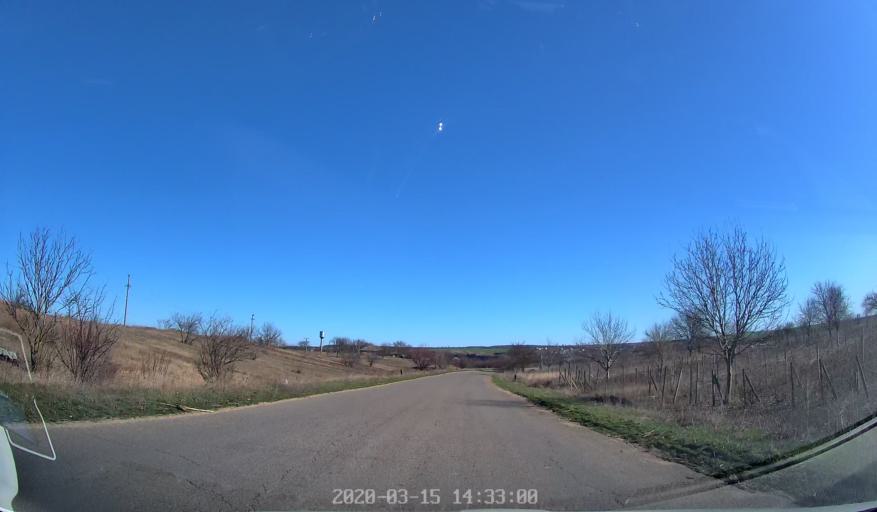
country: MD
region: Orhei
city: Orhei
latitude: 47.3413
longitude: 28.9144
